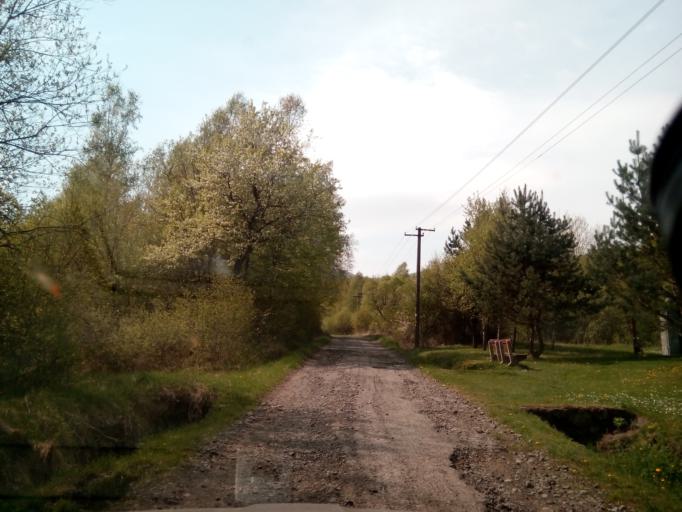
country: SK
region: Presovsky
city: Giraltovce
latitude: 48.9691
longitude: 21.5034
